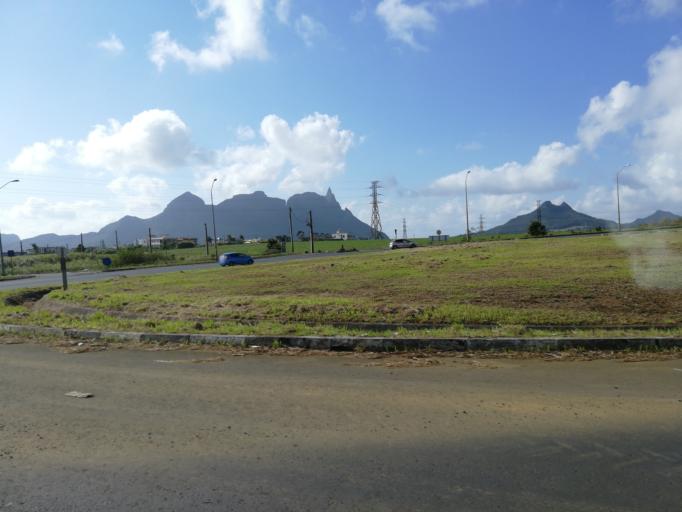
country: MU
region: Moka
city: Verdun
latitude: -20.2246
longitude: 57.5580
